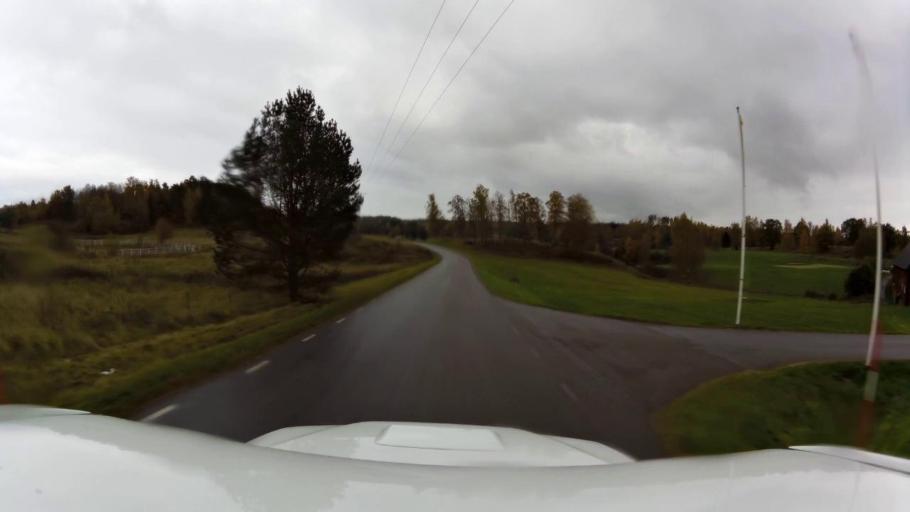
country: SE
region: OEstergoetland
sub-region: Linkopings Kommun
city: Ljungsbro
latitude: 58.5277
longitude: 15.5206
